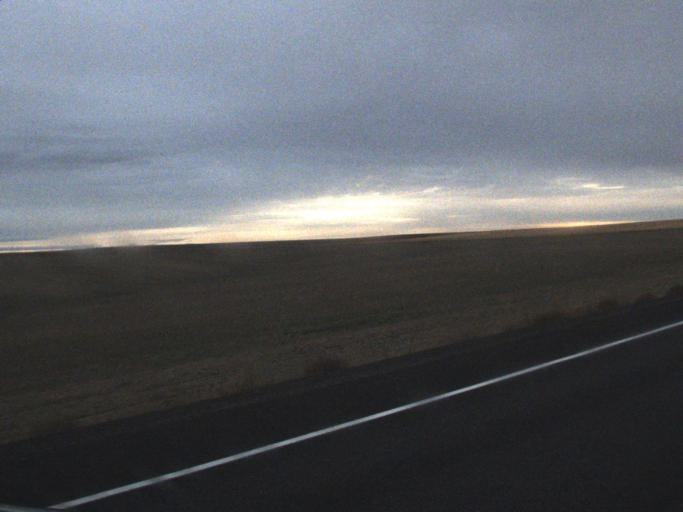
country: US
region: Washington
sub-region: Franklin County
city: Connell
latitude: 46.7944
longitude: -118.6776
